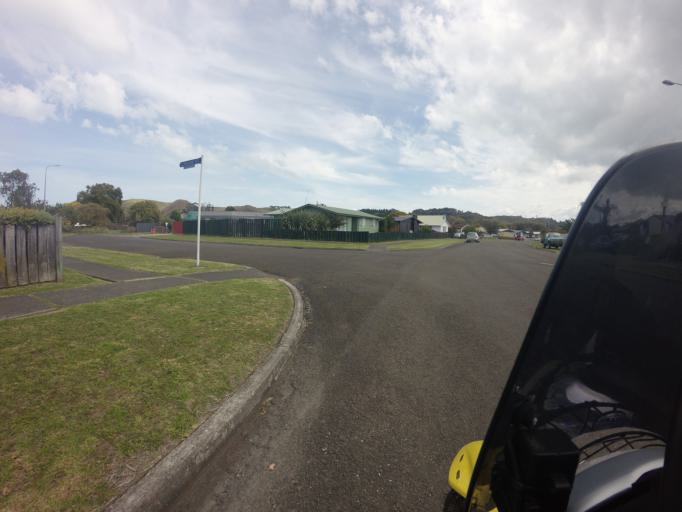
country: NZ
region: Gisborne
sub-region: Gisborne District
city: Gisborne
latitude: -38.6769
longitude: 178.0524
